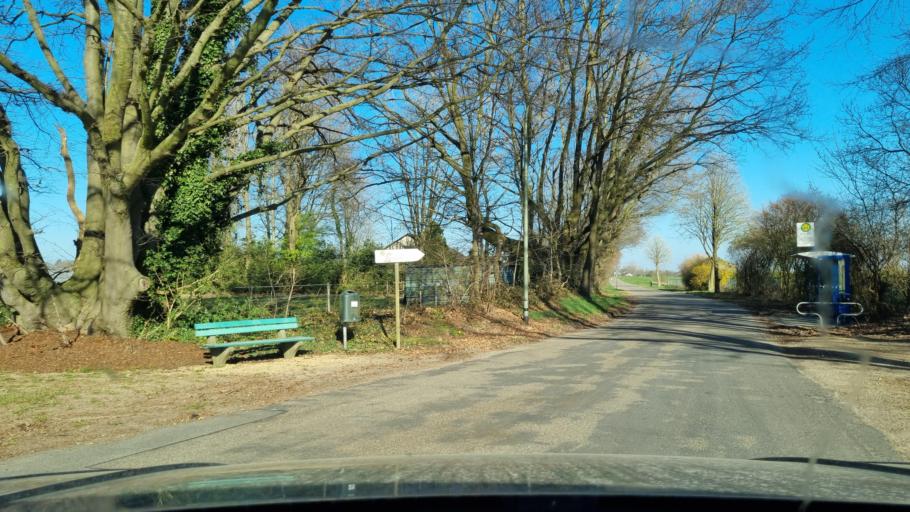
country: DE
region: North Rhine-Westphalia
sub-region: Regierungsbezirk Dusseldorf
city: Goch
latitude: 51.7155
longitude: 6.1296
